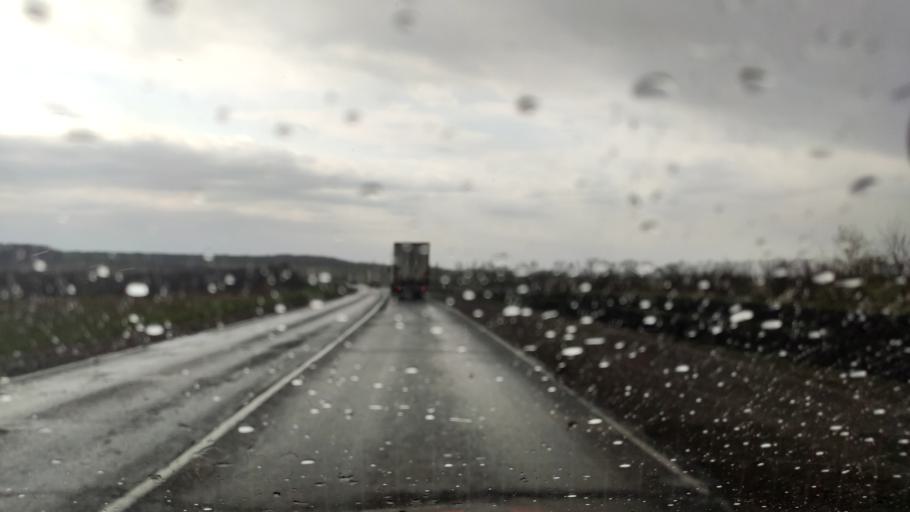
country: RU
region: Voronezj
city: Nizhnedevitsk
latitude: 51.5758
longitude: 38.3224
